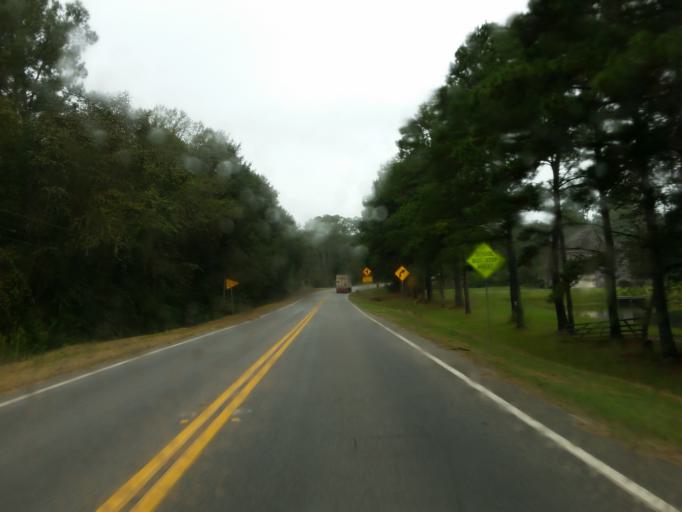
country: US
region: Georgia
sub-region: Berrien County
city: Ray City
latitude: 31.0737
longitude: -83.2063
